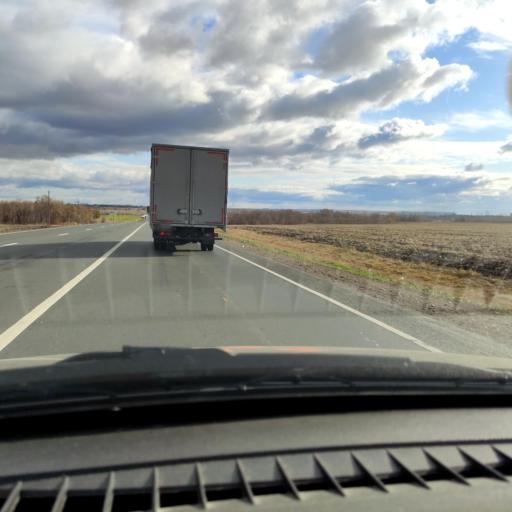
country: RU
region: Samara
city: Varlamovo
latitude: 53.2115
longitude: 48.4646
